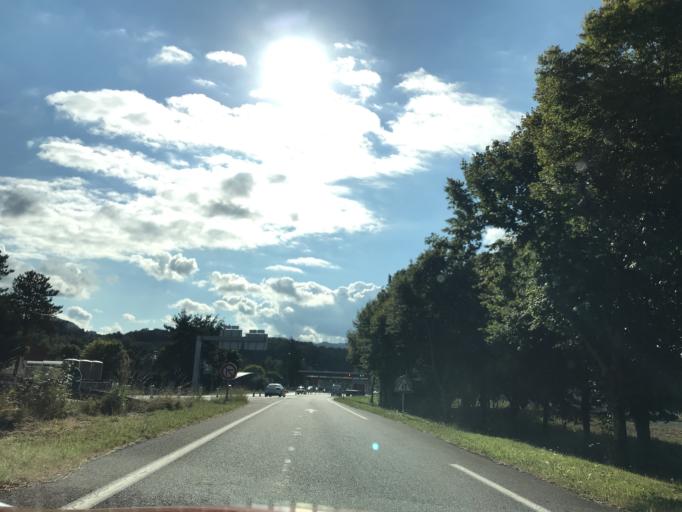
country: FR
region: Auvergne
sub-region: Departement du Puy-de-Dome
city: Peschadoires
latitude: 45.8606
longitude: 3.5009
